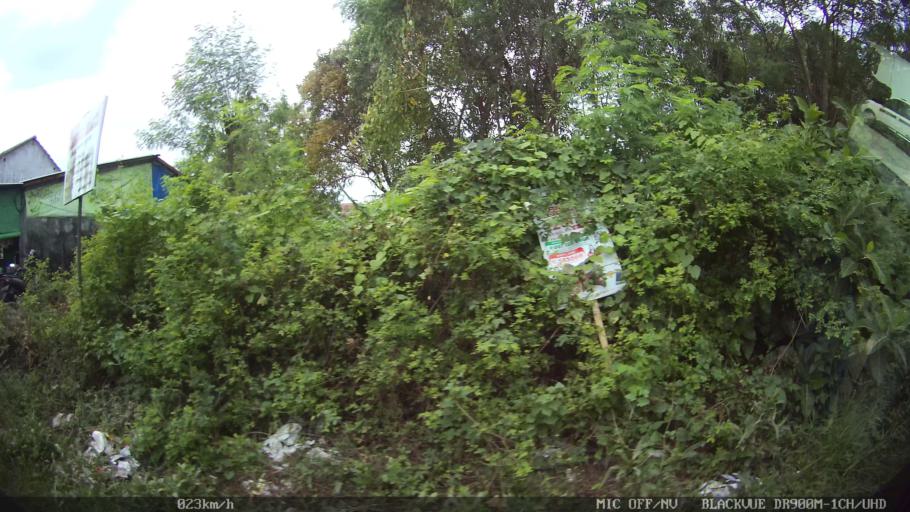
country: ID
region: Daerah Istimewa Yogyakarta
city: Gamping Lor
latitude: -7.7762
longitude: 110.3368
